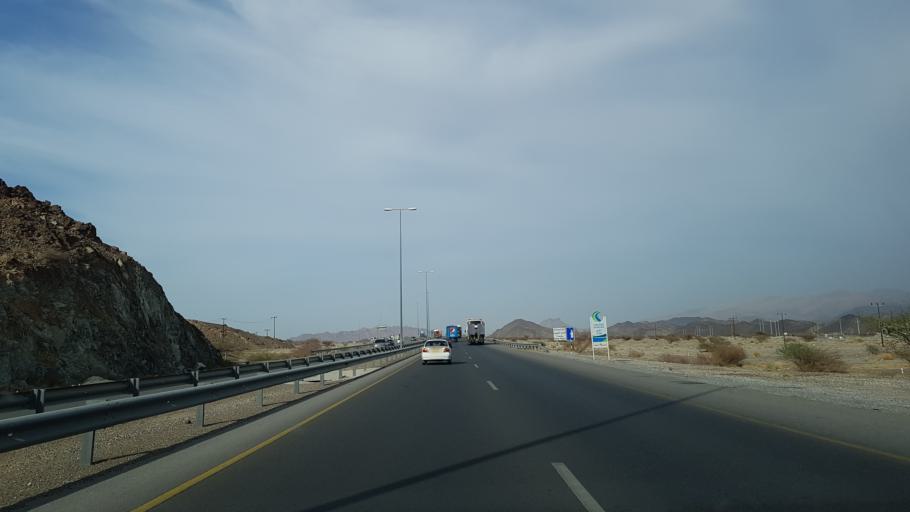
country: OM
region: Muhafazat ad Dakhiliyah
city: Sufalat Sama'il
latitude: 23.3708
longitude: 58.0447
